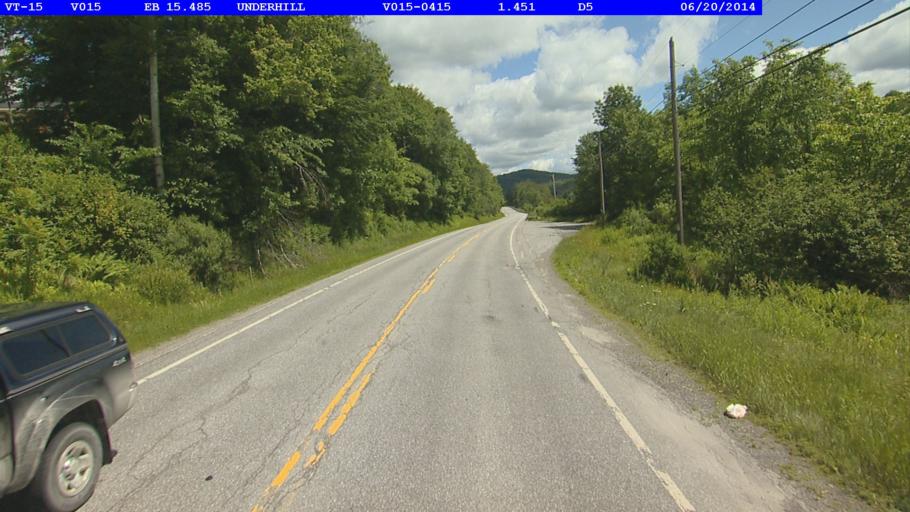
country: US
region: Vermont
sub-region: Chittenden County
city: Jericho
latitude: 44.5452
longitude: -72.9482
